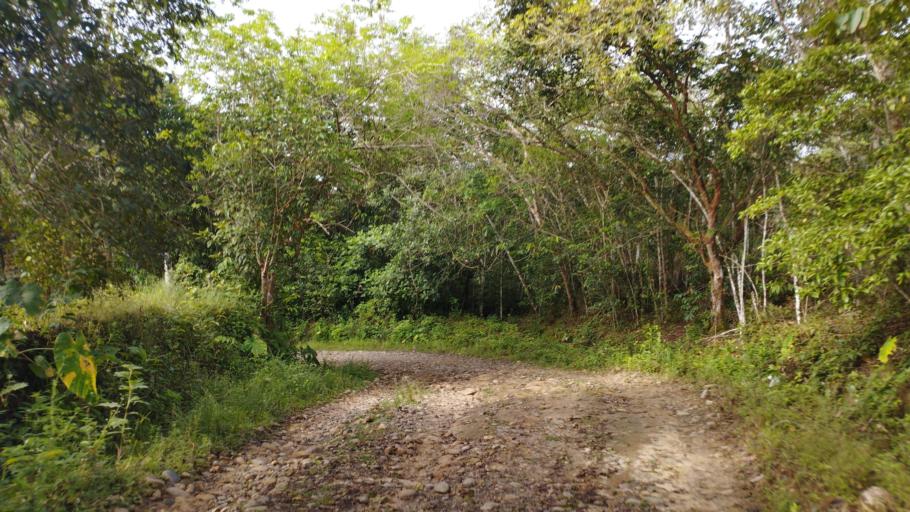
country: CO
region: Casanare
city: Sabanalarga
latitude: 4.7614
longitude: -73.0810
